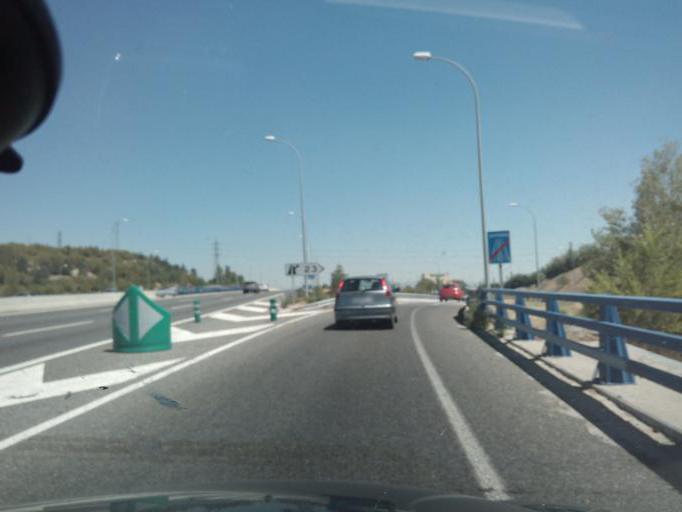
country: ES
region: Madrid
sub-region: Provincia de Madrid
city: San Sebastian de los Reyes
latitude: 40.5778
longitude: -3.5854
